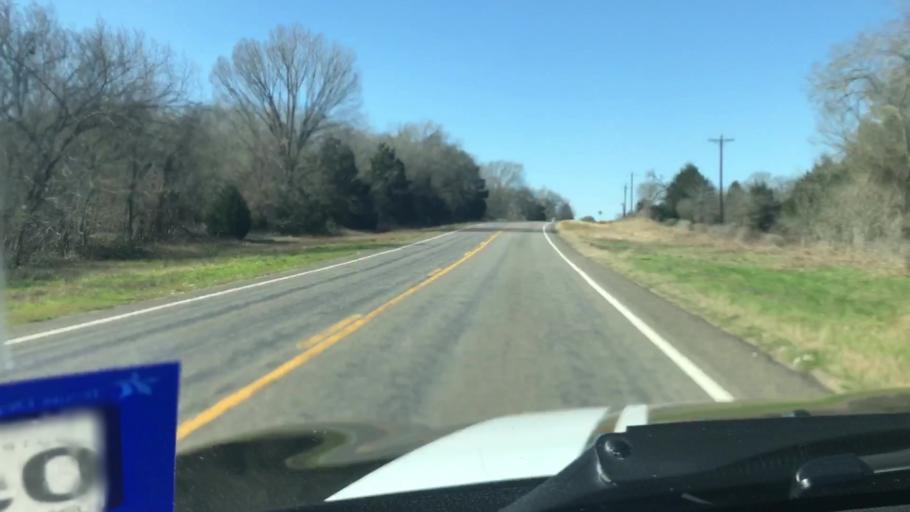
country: US
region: Texas
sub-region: Robertson County
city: Calvert
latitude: 30.8847
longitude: -96.7646
